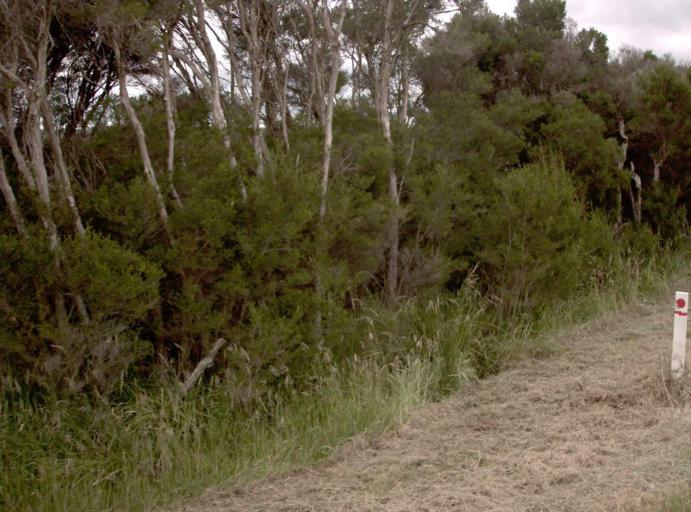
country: AU
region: Victoria
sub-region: Bass Coast
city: North Wonthaggi
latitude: -38.5911
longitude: 145.6137
